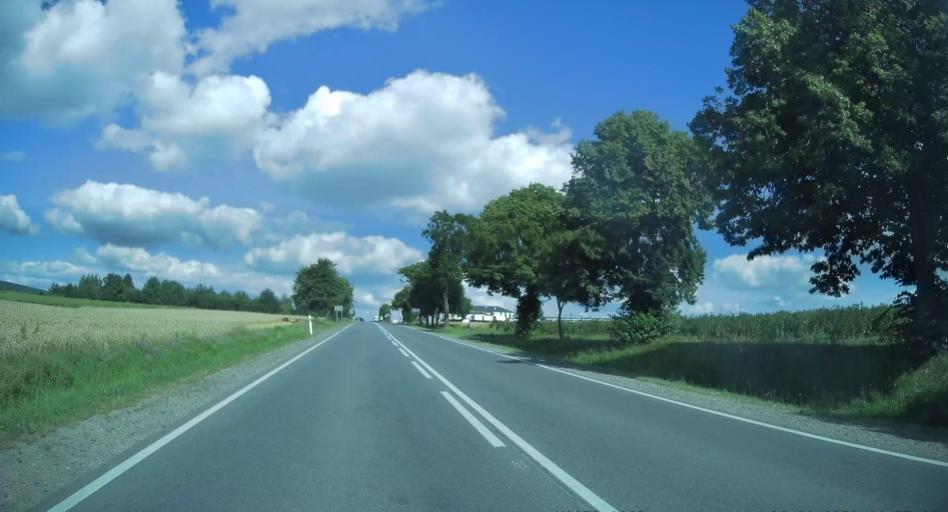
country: PL
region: Swietokrzyskie
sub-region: Powiat opatowski
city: Backowice
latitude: 50.7989
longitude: 21.2285
